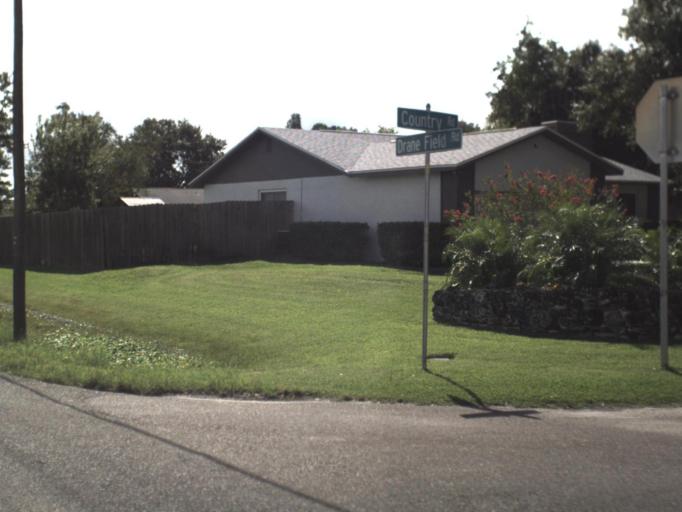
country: US
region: Florida
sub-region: Polk County
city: Medulla
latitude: 27.9967
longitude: -81.9900
